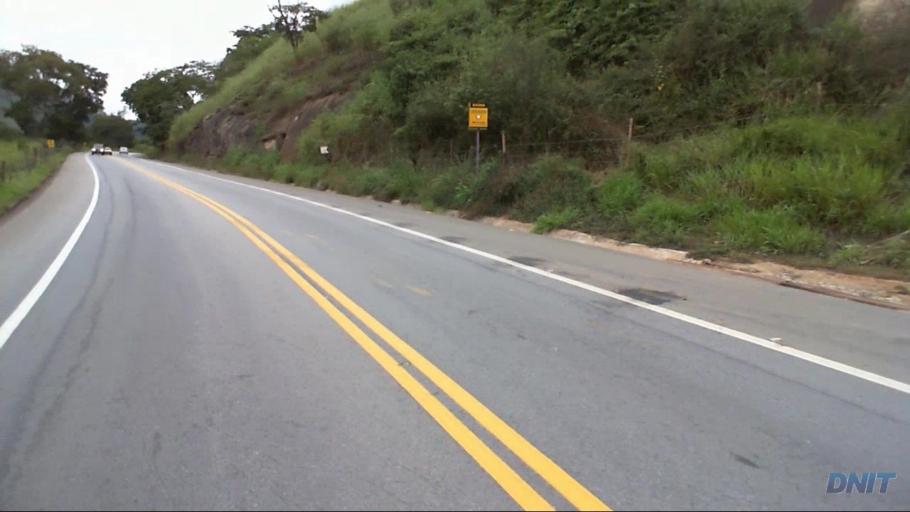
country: BR
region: Minas Gerais
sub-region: Timoteo
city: Timoteo
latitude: -19.5841
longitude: -42.7289
